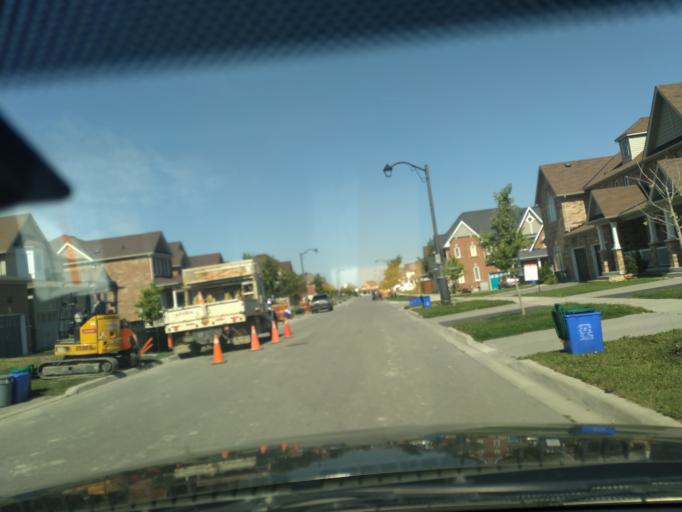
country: CA
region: Ontario
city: Keswick
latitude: 44.2006
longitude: -79.4630
